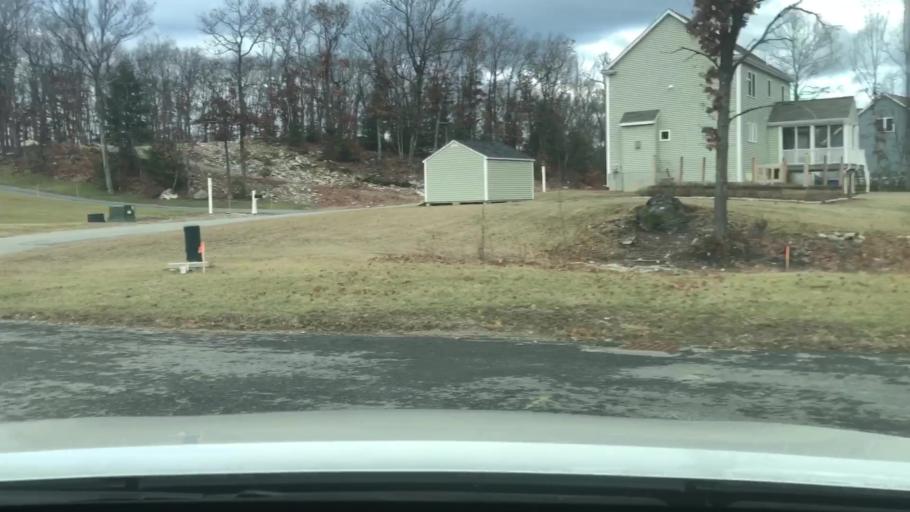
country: US
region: Rhode Island
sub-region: Providence County
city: Woonsocket
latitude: 42.0332
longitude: -71.5143
